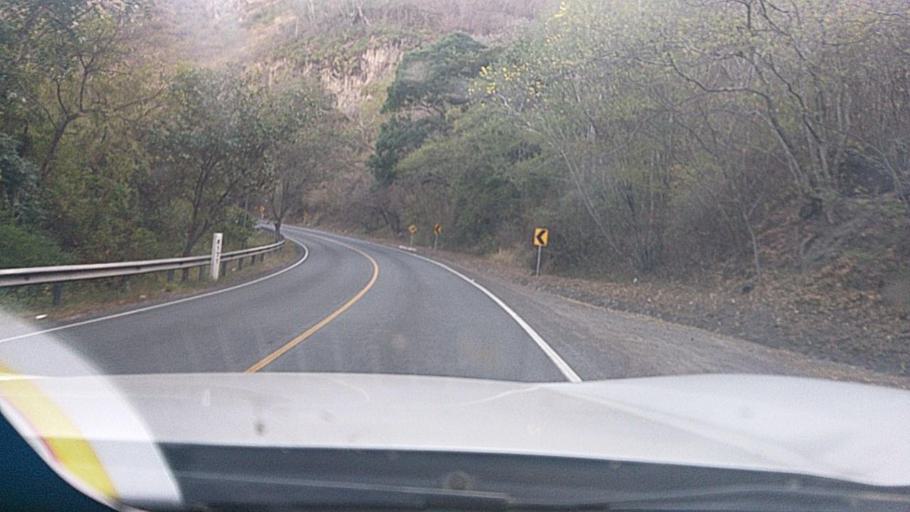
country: NI
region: Esteli
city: Condega
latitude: 13.2712
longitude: -86.3559
